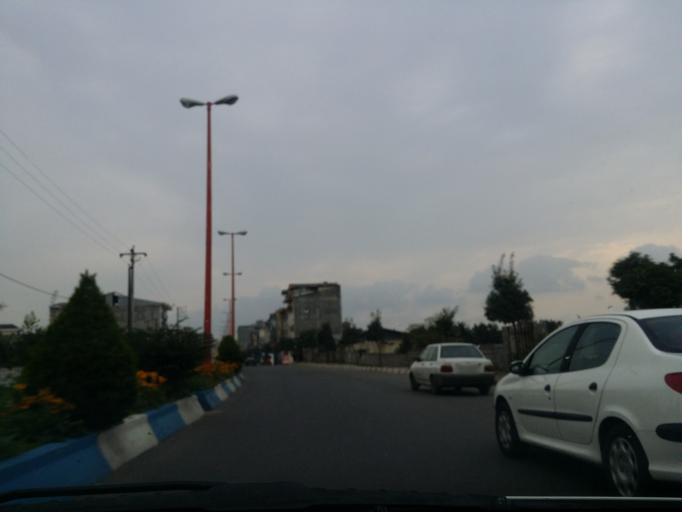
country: IR
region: Mazandaran
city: `Abbasabad
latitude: 36.7179
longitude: 51.1028
